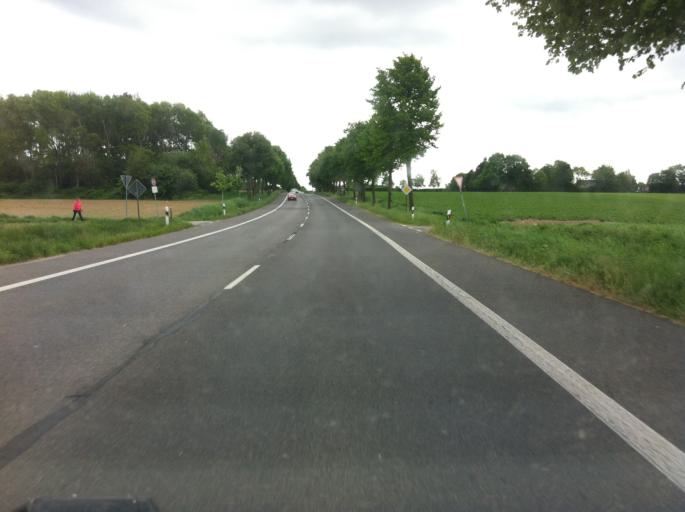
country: DE
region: North Rhine-Westphalia
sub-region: Regierungsbezirk Dusseldorf
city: Niederkruchten
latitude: 51.2152
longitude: 6.2096
